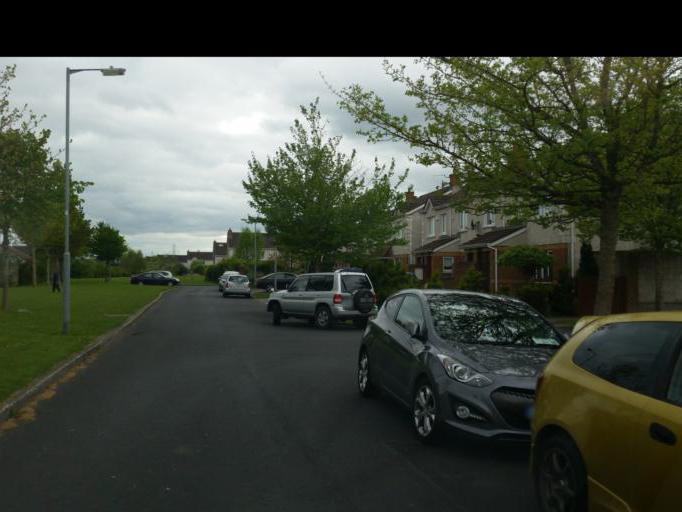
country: IE
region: Leinster
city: Hartstown
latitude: 53.3972
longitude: -6.4221
